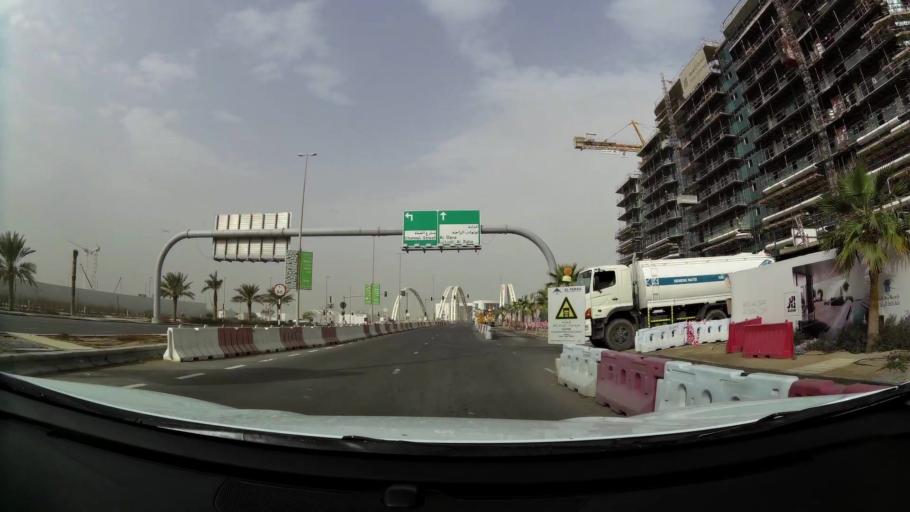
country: AE
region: Abu Dhabi
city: Abu Dhabi
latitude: 24.4484
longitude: 54.5999
